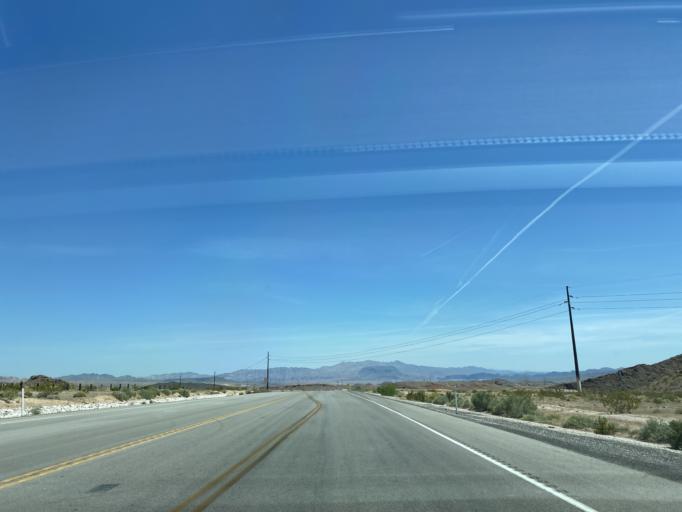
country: US
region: Nevada
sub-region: Clark County
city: Nellis Air Force Base
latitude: 36.2048
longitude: -114.9443
